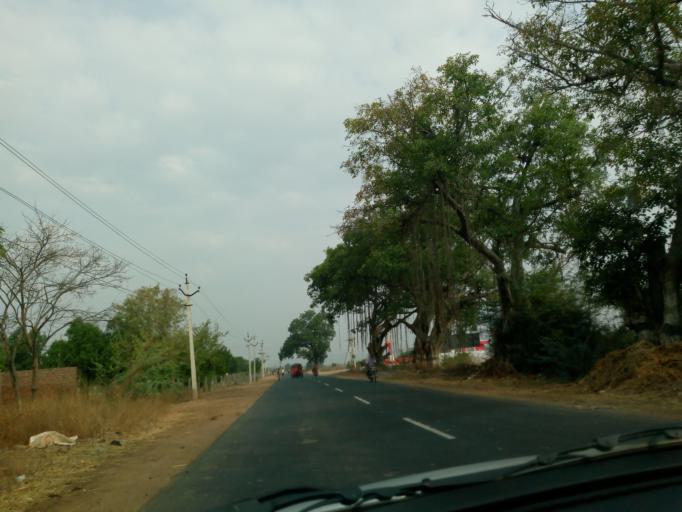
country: IN
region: Andhra Pradesh
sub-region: Prakasam
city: Diguvametta
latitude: 15.3731
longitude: 78.8785
